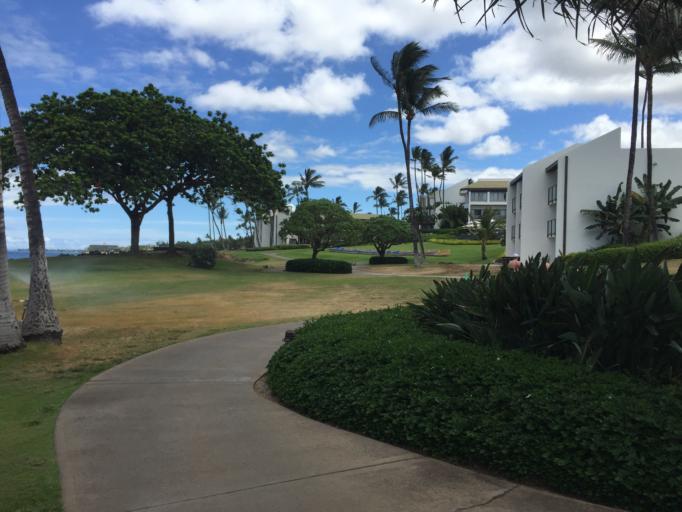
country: US
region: Hawaii
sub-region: Maui County
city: Kihei
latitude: 20.6862
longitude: -156.4444
